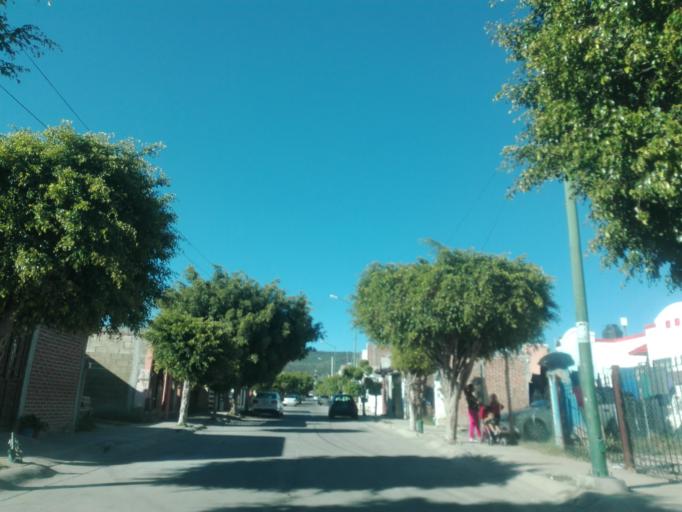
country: MX
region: Guanajuato
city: Leon
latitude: 21.1924
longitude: -101.6755
